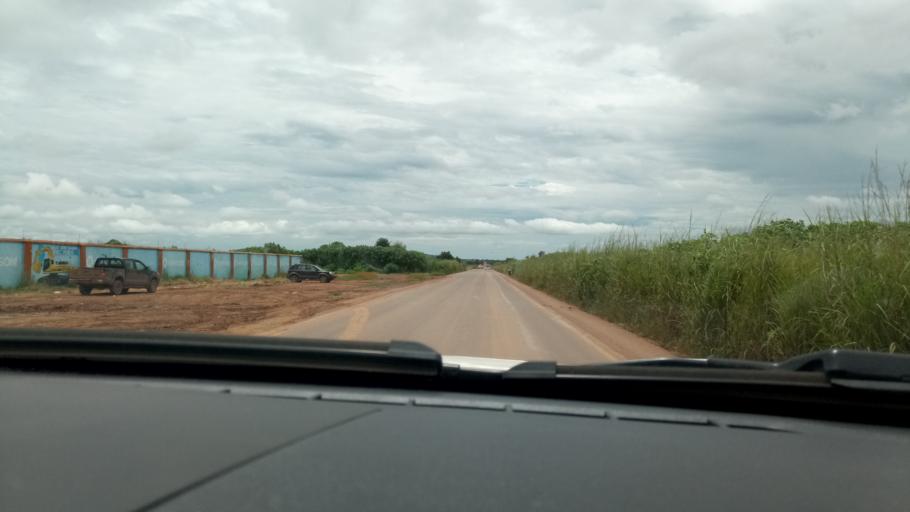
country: CD
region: Katanga
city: Lubumbashi
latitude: -11.5727
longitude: 27.5414
